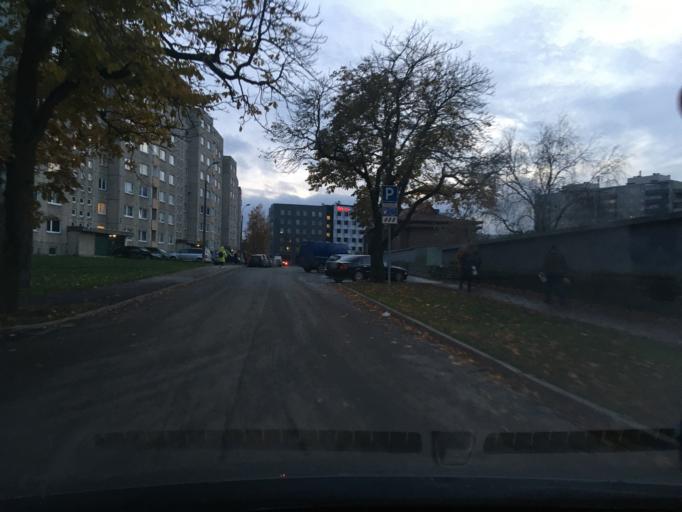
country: EE
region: Harju
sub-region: Tallinna linn
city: Tallinn
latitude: 59.4294
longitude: 24.7671
